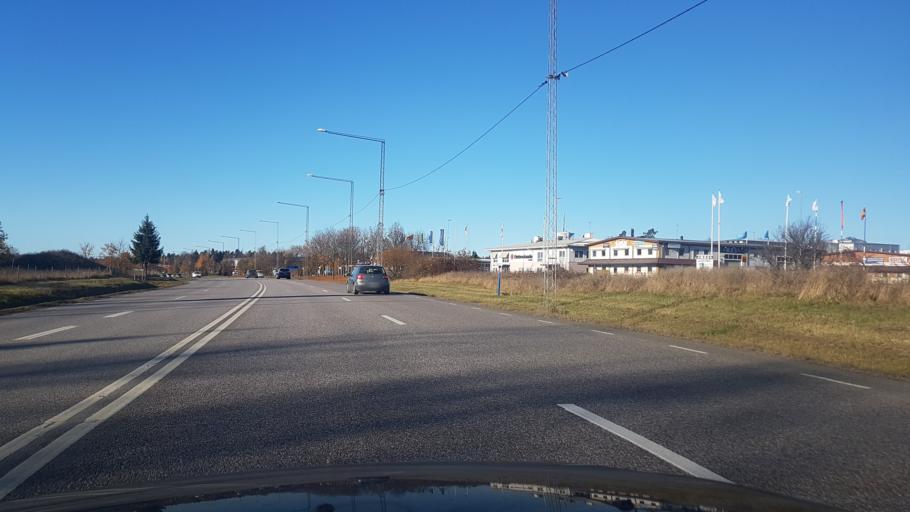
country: SE
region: Stockholm
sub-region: Sigtuna Kommun
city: Rosersberg
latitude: 59.6126
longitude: 17.8829
